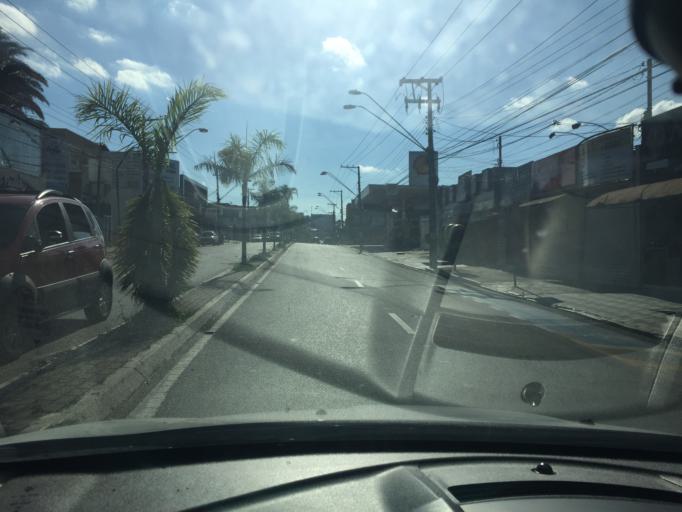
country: BR
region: Sao Paulo
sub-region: Varzea Paulista
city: Varzea Paulista
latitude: -23.2128
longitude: -46.8352
